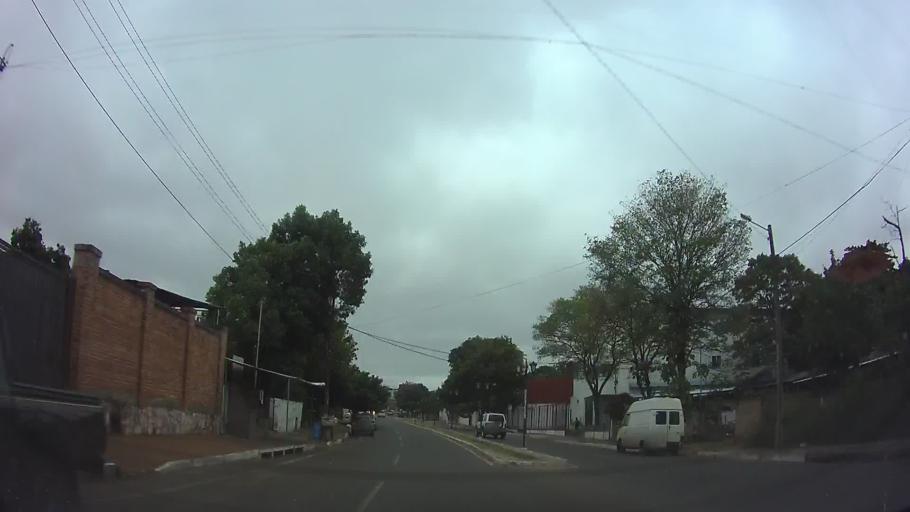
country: PY
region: Asuncion
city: Asuncion
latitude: -25.3080
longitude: -57.6262
